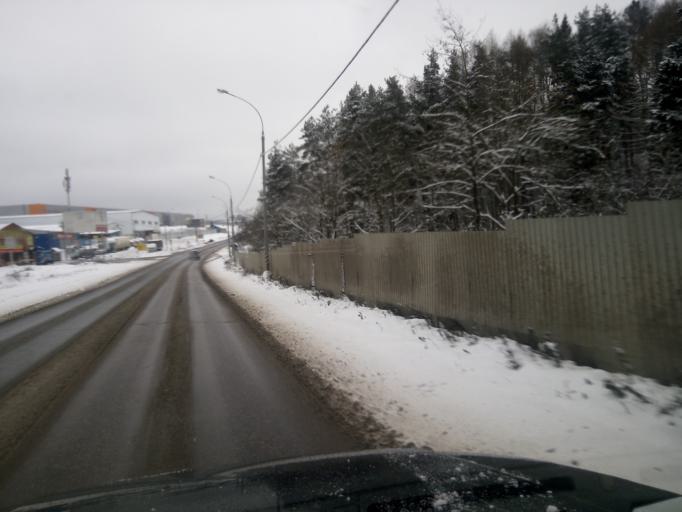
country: RU
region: Moskovskaya
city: Skhodnya
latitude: 55.9672
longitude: 37.3099
